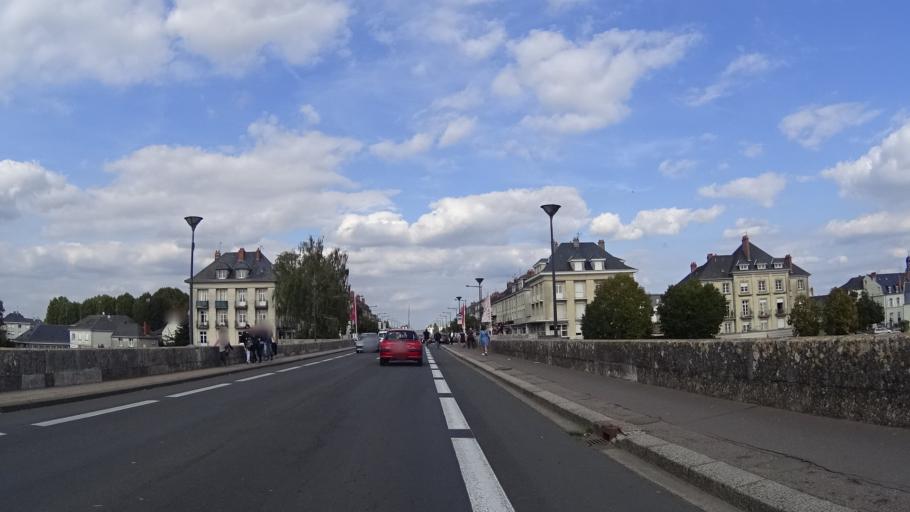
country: FR
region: Pays de la Loire
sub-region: Departement de Maine-et-Loire
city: Saumur
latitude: 47.2629
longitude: -0.0749
